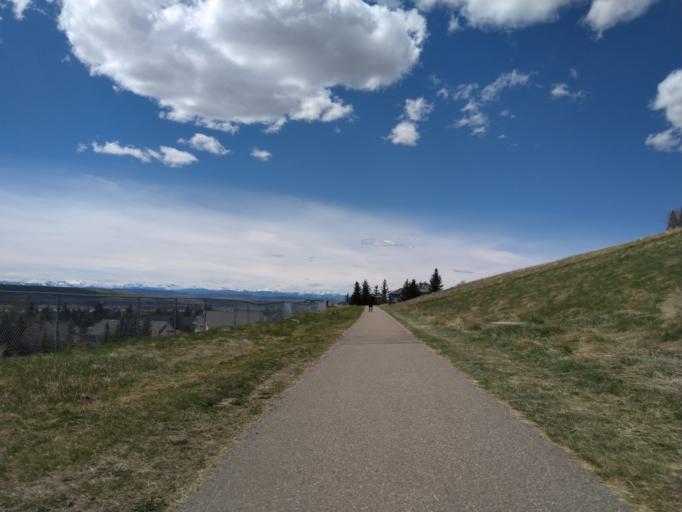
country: CA
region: Alberta
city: Calgary
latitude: 51.0206
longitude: -114.1740
